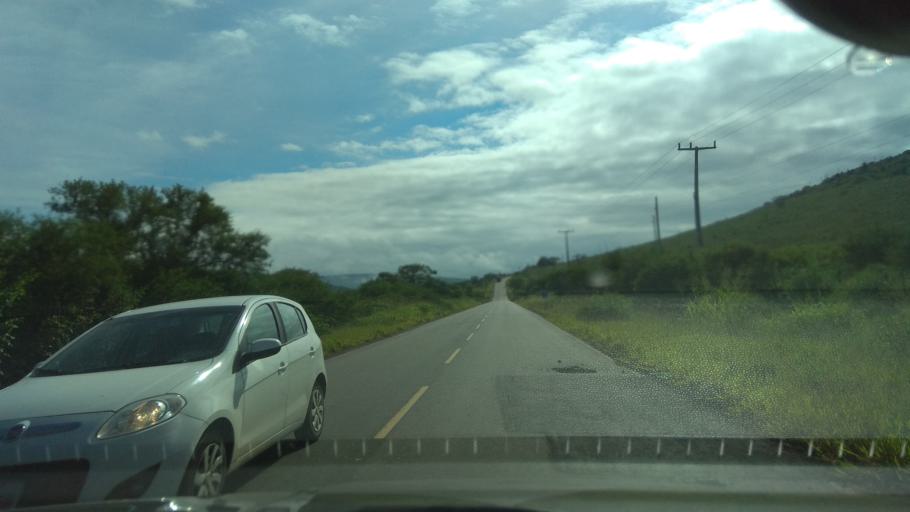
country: BR
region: Bahia
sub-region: Santa Ines
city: Santa Ines
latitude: -13.3594
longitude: -39.8813
